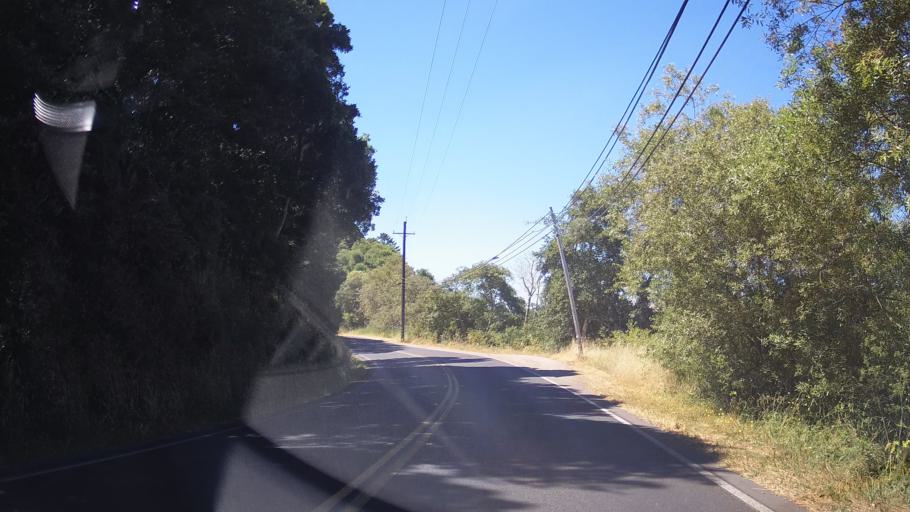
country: US
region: California
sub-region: Marin County
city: Inverness
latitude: 38.0900
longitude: -122.8441
